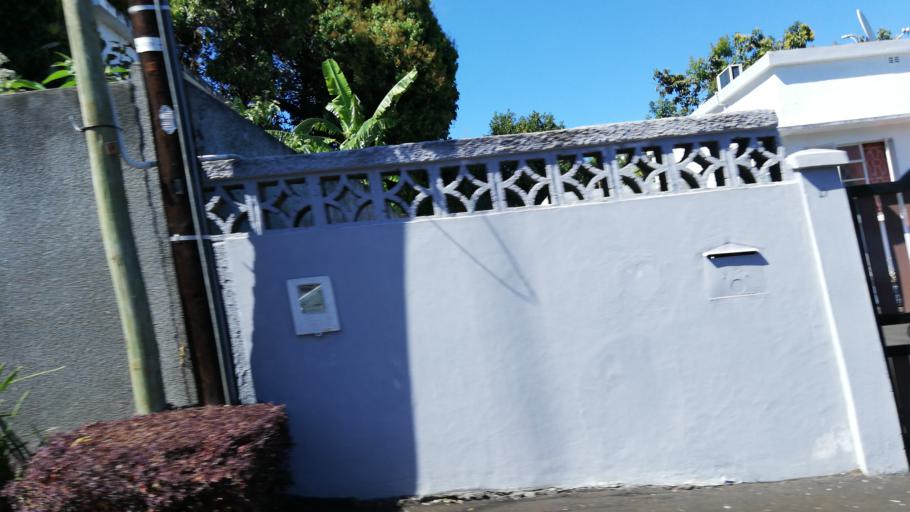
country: MU
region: Plaines Wilhems
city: Ebene
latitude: -20.2353
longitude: 57.4750
